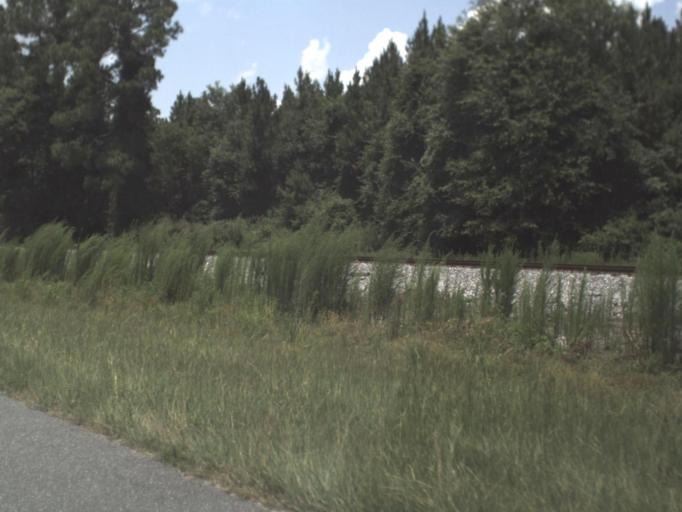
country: US
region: Florida
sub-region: Columbia County
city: Five Points
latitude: 30.2616
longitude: -82.6861
